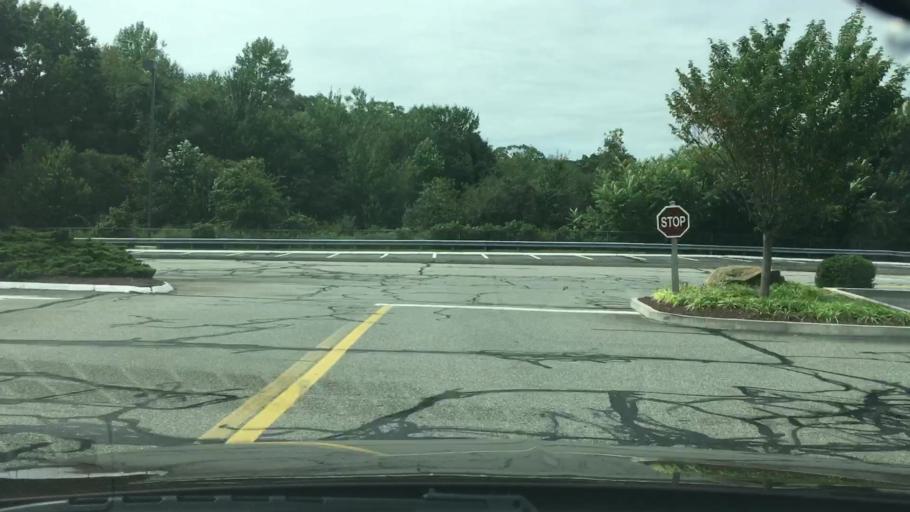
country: US
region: Connecticut
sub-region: Middlesex County
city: Westbrook Center
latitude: 41.2884
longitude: -72.4315
